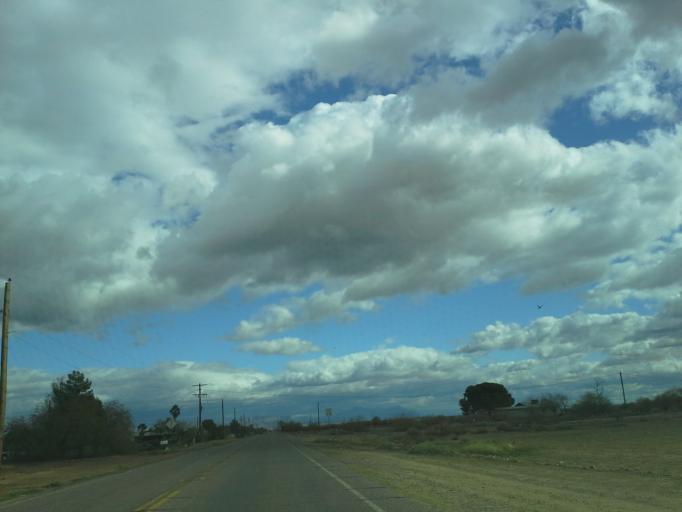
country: US
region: Arizona
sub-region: Maricopa County
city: Scottsdale
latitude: 33.4805
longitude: -111.8553
